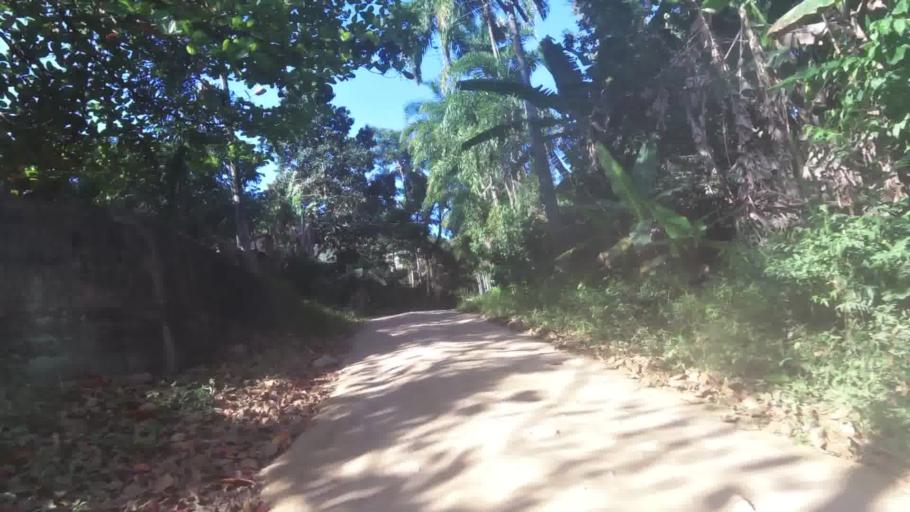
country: BR
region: Espirito Santo
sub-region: Iconha
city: Iconha
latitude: -20.7578
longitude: -40.8180
